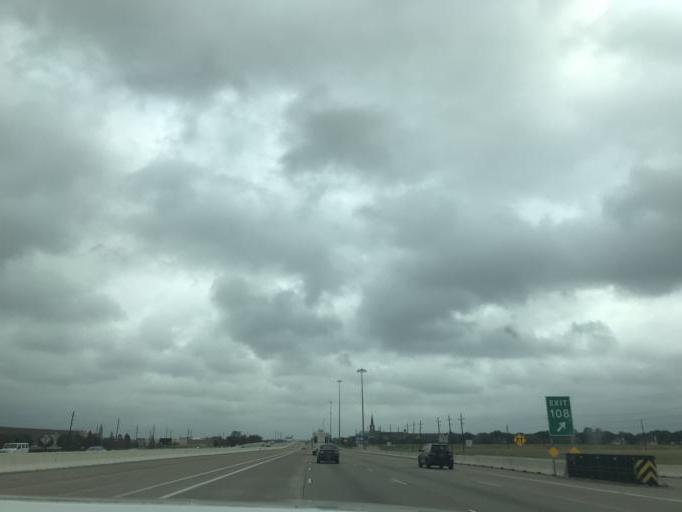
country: US
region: Texas
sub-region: Fort Bend County
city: New Territory
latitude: 29.5826
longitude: -95.6448
